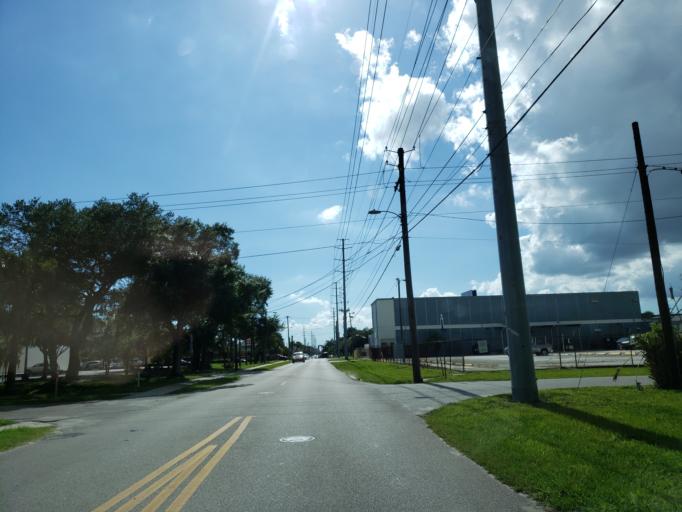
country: US
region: Florida
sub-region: Hillsborough County
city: Tampa
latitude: 27.9595
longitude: -82.5029
